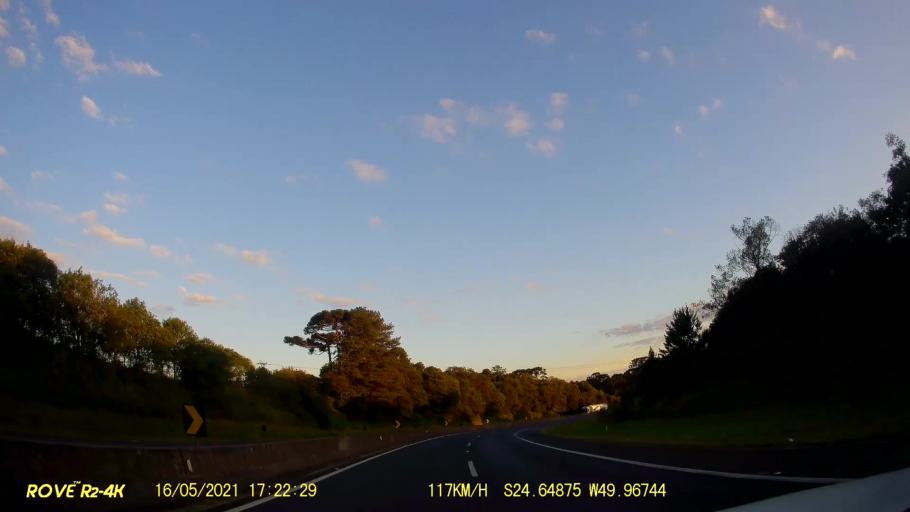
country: BR
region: Parana
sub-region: Pirai Do Sul
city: Pirai do Sul
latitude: -24.6493
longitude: -49.9673
